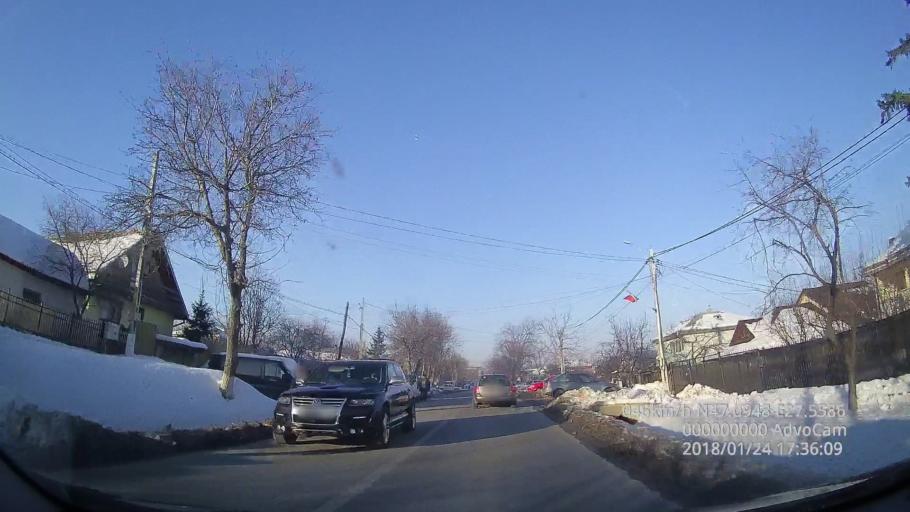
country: RO
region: Iasi
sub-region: Comuna Ciurea
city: Lunca Cetatuii
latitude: 47.0952
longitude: 27.5587
